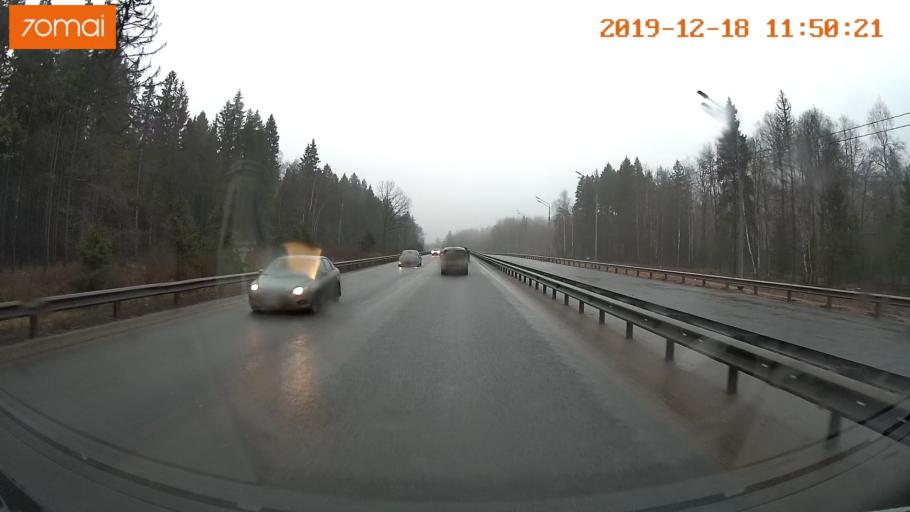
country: RU
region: Moskovskaya
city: Yershovo
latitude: 55.7850
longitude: 36.9180
